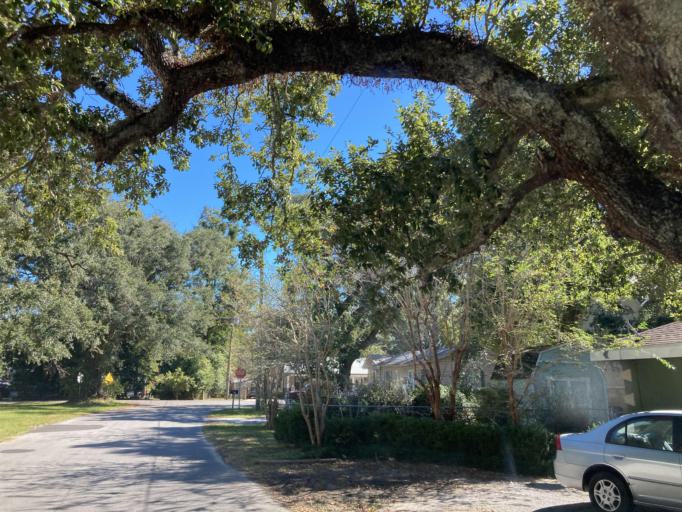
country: US
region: Mississippi
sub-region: Jackson County
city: Ocean Springs
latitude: 30.4114
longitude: -88.8197
